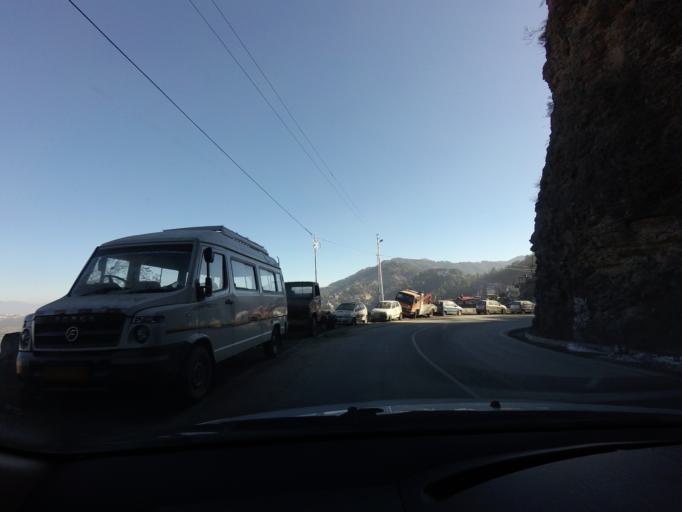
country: IN
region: Himachal Pradesh
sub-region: Shimla
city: Shimla
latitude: 31.1082
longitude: 77.2088
